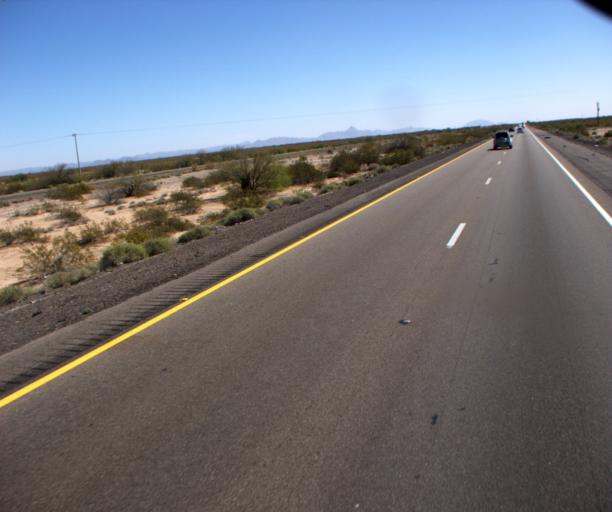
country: US
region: Arizona
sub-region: La Paz County
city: Salome
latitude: 33.5866
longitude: -113.4715
